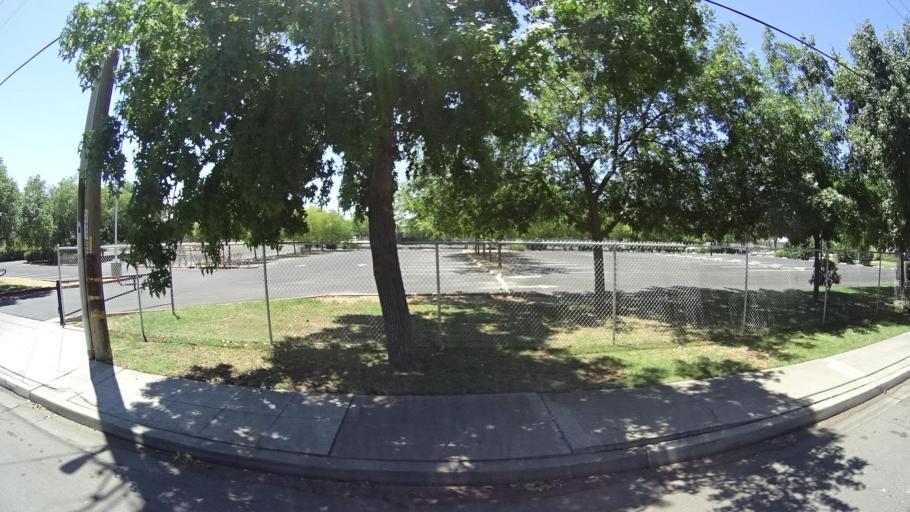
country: US
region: California
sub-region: Fresno County
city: Fresno
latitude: 36.7886
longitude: -119.7923
